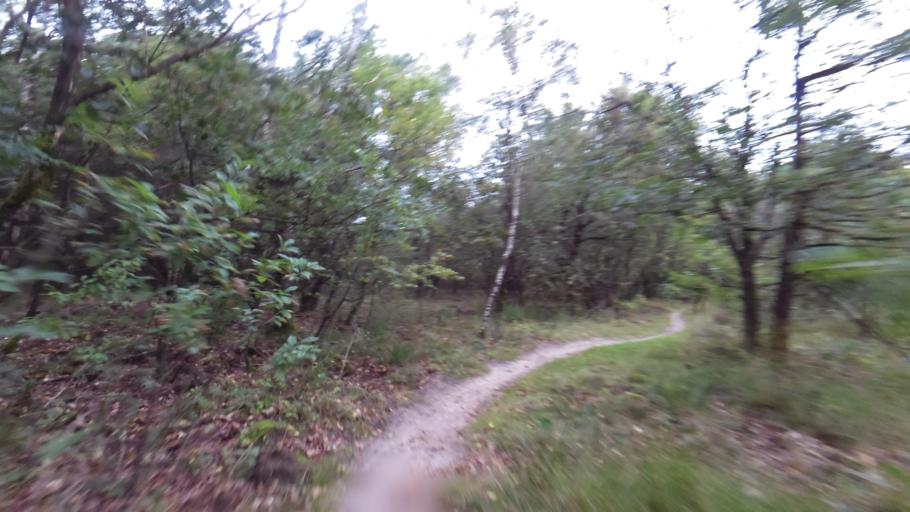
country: NL
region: Gelderland
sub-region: Gemeente Ede
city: Harskamp
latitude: 52.1812
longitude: 5.8253
